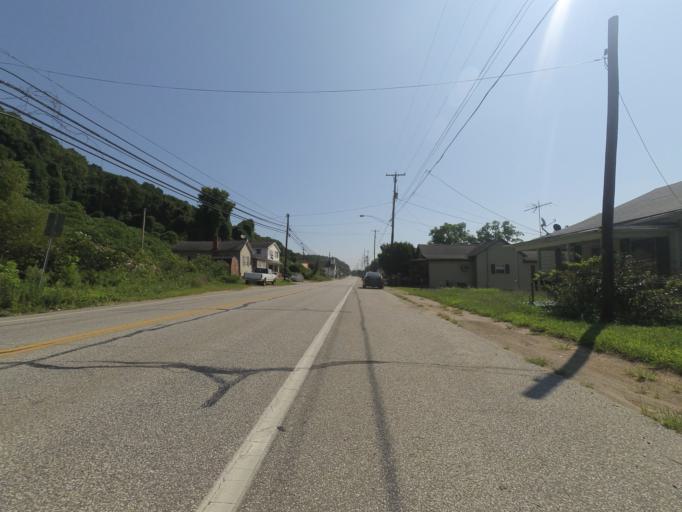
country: US
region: West Virginia
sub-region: Cabell County
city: Huntington
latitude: 38.4317
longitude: -82.4355
